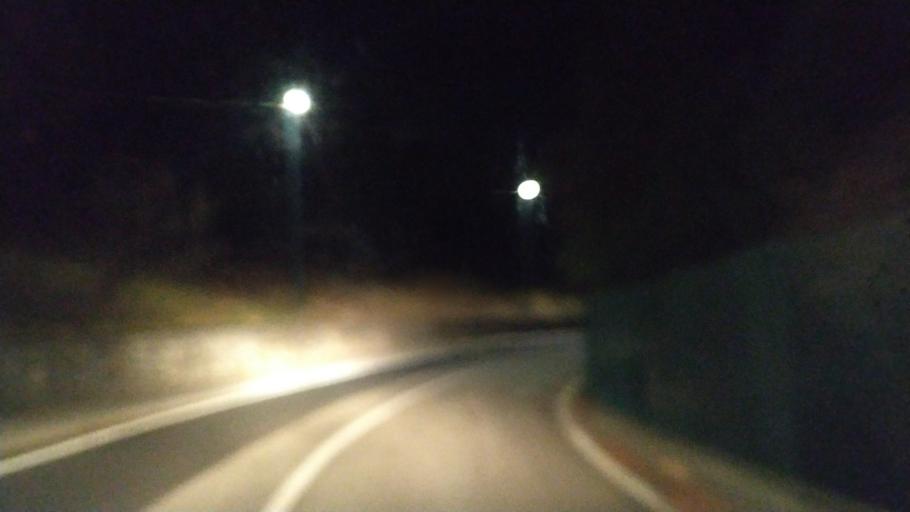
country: IT
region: Piedmont
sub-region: Provincia di Biella
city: Occhieppo Superiore
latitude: 45.5691
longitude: 8.0013
